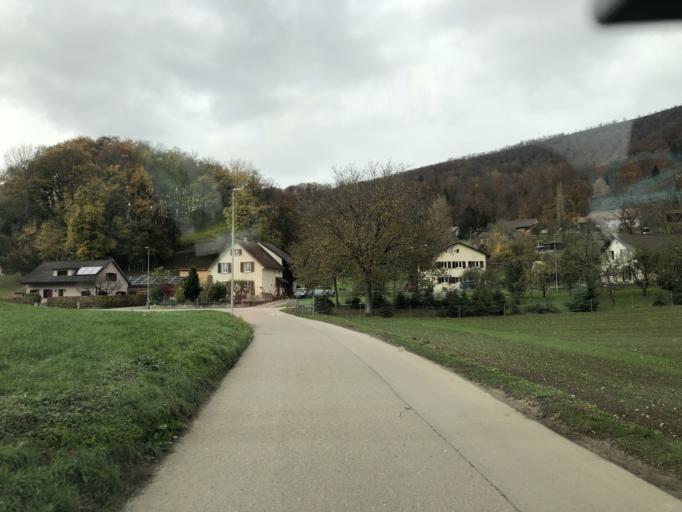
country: CH
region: Aargau
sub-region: Bezirk Baden
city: Neuenhof
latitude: 47.4686
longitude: 8.3435
